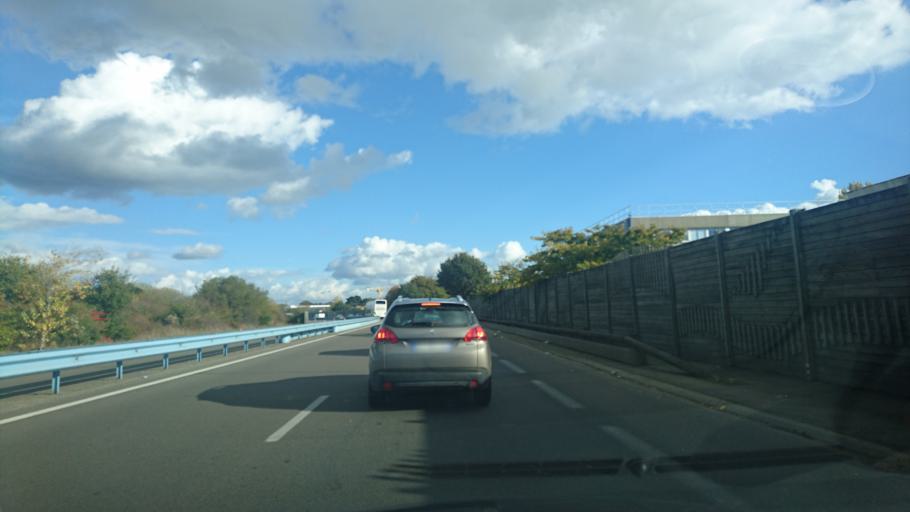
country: FR
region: Pays de la Loire
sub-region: Departement de la Vendee
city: Les Sables-d'Olonne
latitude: 46.5129
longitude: -1.7738
